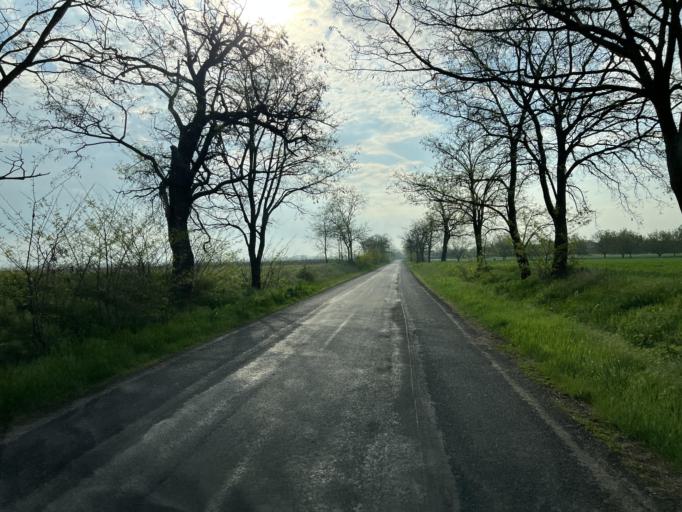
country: HU
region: Pest
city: Cegledbercel
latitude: 47.2149
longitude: 19.7140
